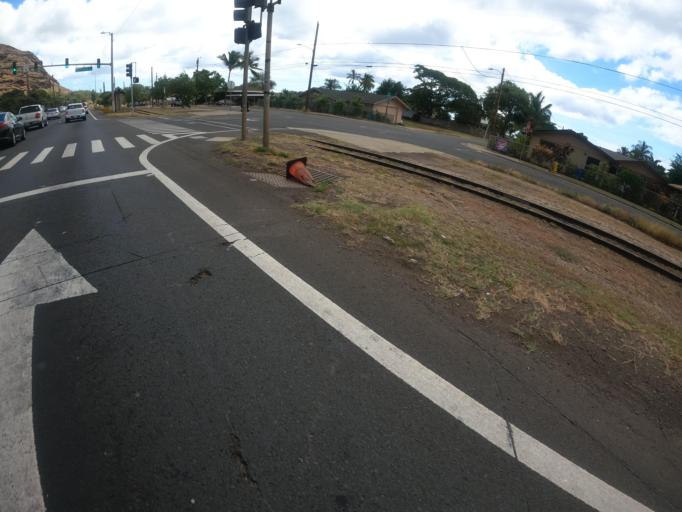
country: US
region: Hawaii
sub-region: Honolulu County
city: Nanakuli
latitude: 21.3722
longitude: -158.1381
